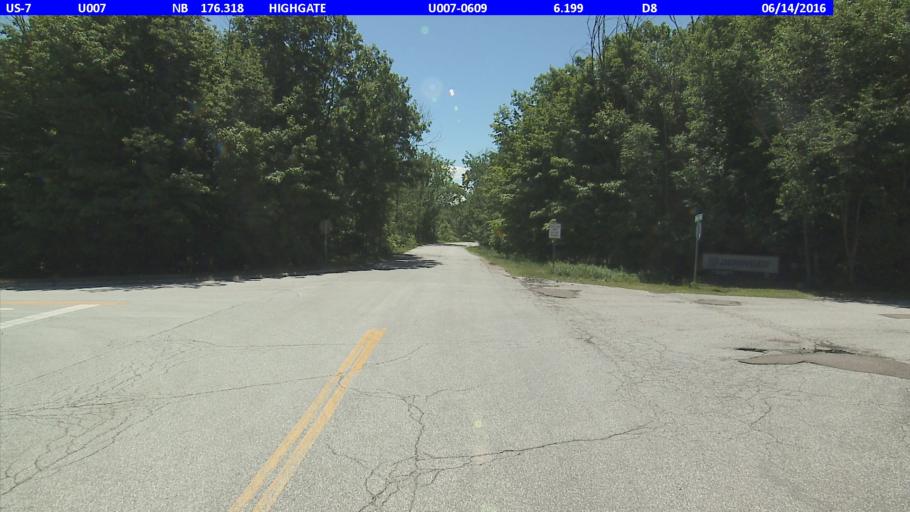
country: US
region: Vermont
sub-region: Franklin County
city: Swanton
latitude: 45.0080
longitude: -73.0878
